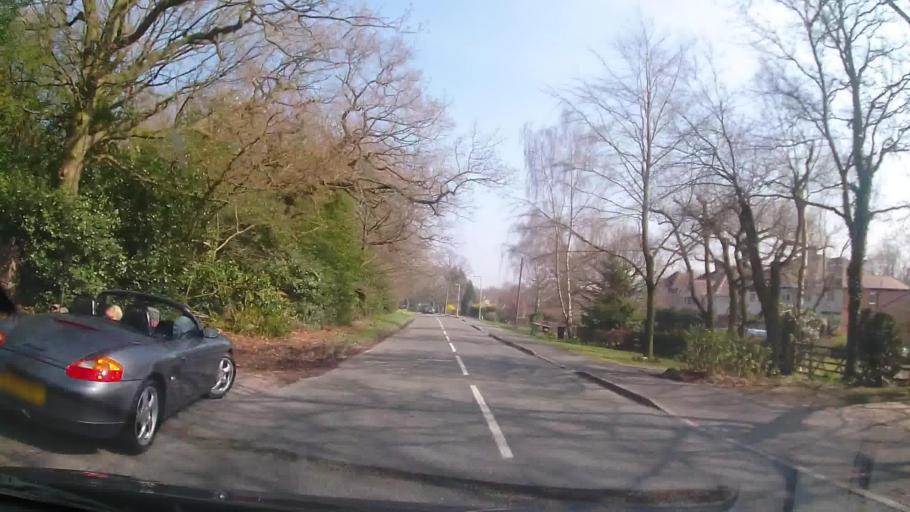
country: GB
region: England
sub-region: Leicestershire
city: Markfield
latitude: 52.6854
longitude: -1.2610
